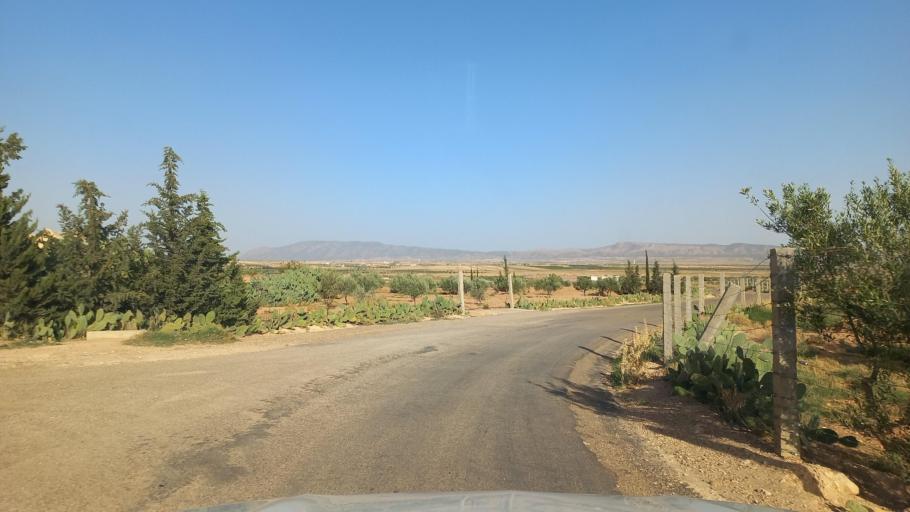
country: TN
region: Al Qasrayn
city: Sbiba
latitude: 35.3794
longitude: 9.0226
